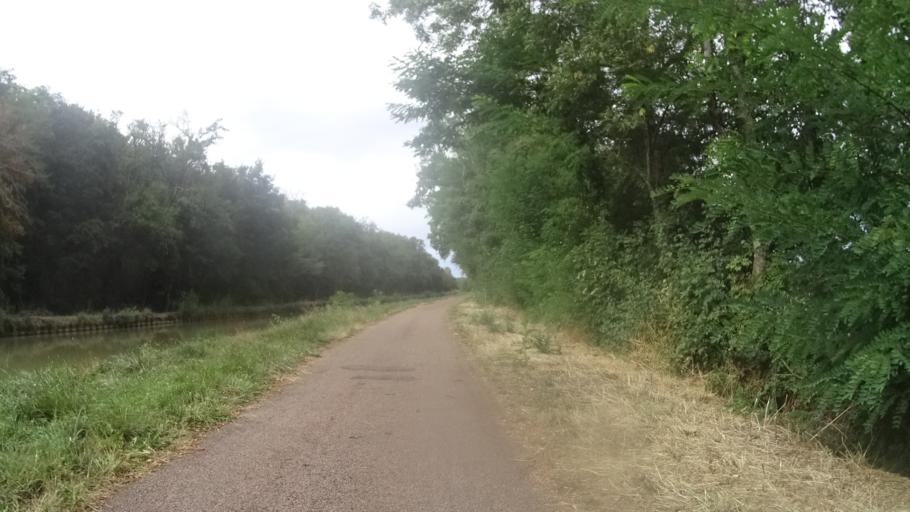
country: FR
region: Bourgogne
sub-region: Departement de la Nievre
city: Sermoise-sur-Loire
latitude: 46.9517
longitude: 3.2005
